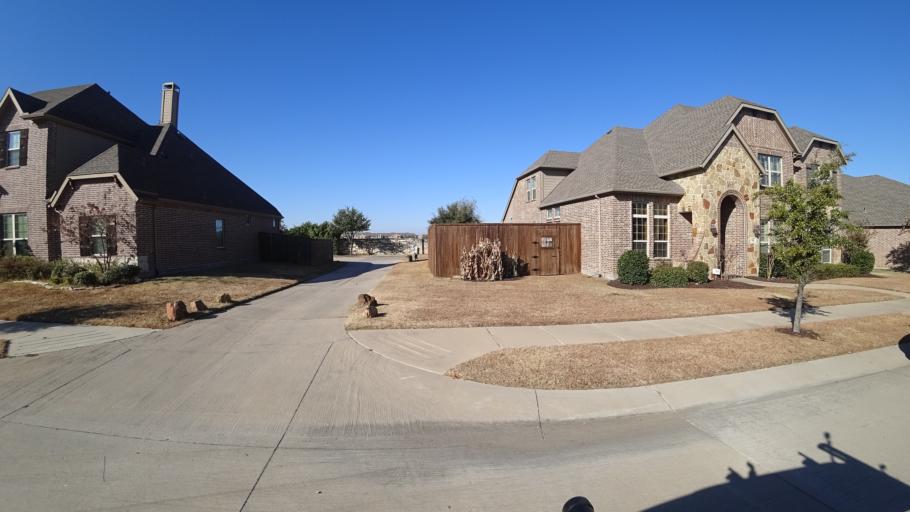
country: US
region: Texas
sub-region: Denton County
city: The Colony
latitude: 33.0412
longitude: -96.9215
